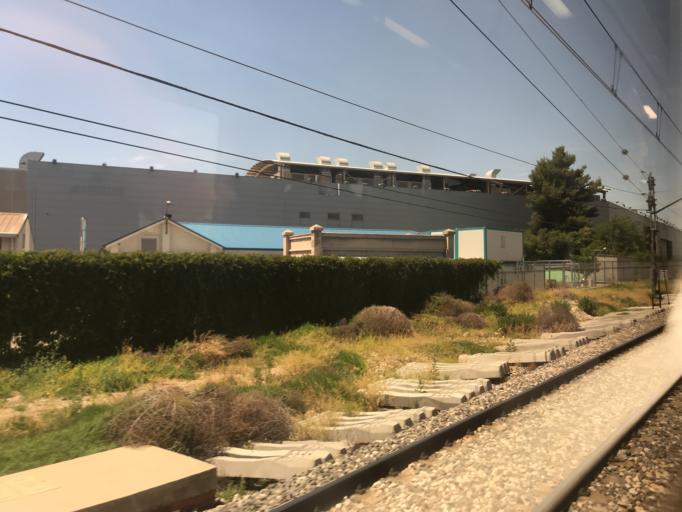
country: ES
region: Madrid
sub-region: Provincia de Madrid
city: Getafe
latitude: 40.3010
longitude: -3.7071
